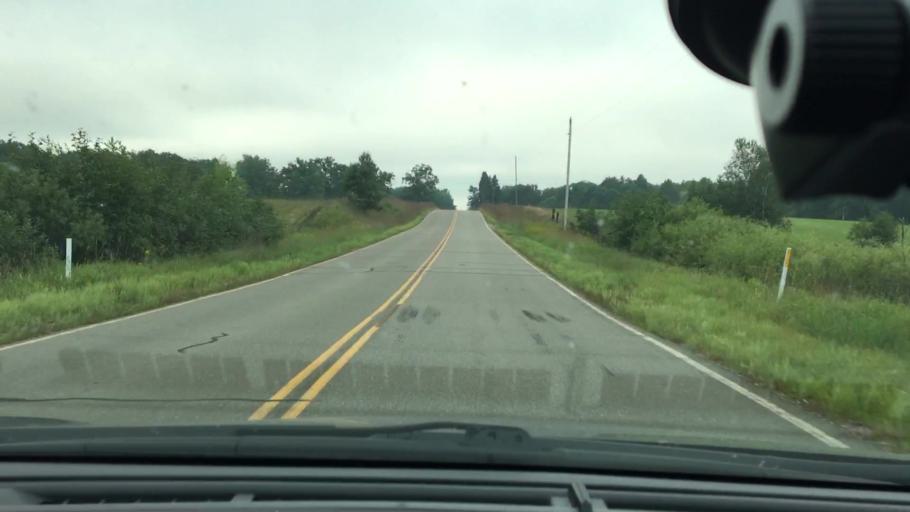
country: US
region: Minnesota
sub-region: Crow Wing County
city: Cross Lake
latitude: 46.6478
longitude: -94.0095
